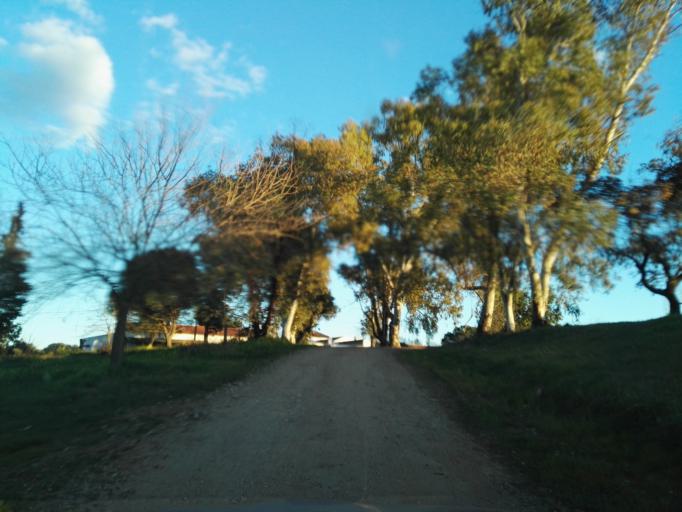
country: PT
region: Castelo Branco
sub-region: Idanha-A-Nova
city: Idanha-a-Nova
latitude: 39.8634
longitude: -7.1344
